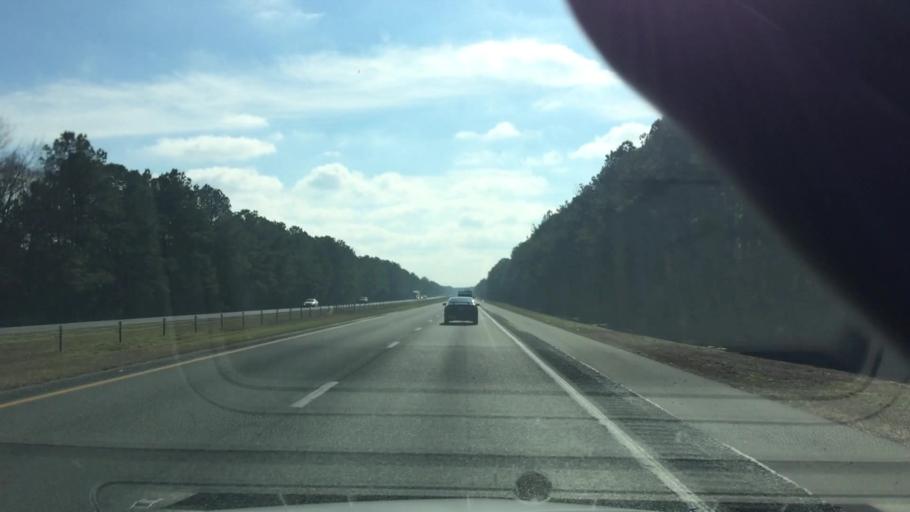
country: US
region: North Carolina
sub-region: Duplin County
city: Wallace
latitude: 34.7284
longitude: -77.9450
